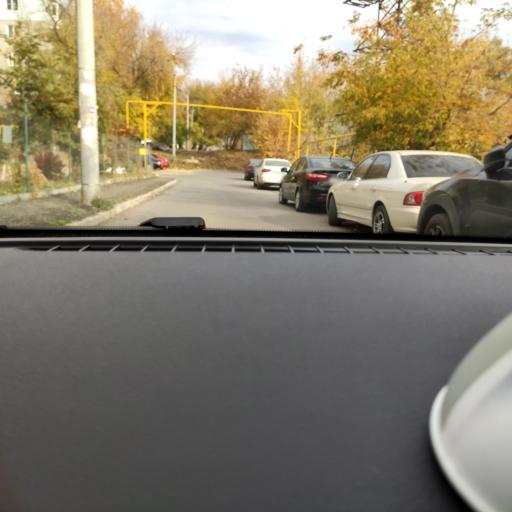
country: RU
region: Samara
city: Samara
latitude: 53.2101
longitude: 50.2081
